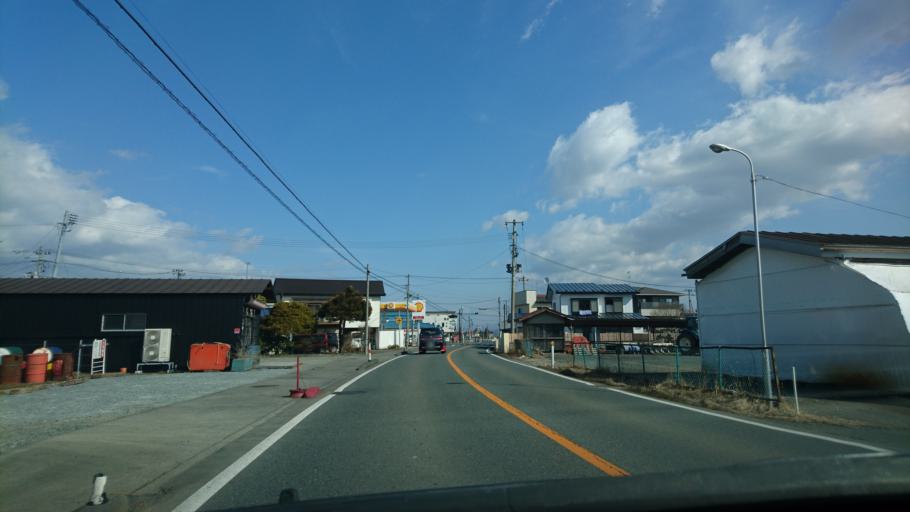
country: JP
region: Iwate
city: Morioka-shi
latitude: 39.5676
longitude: 141.1084
